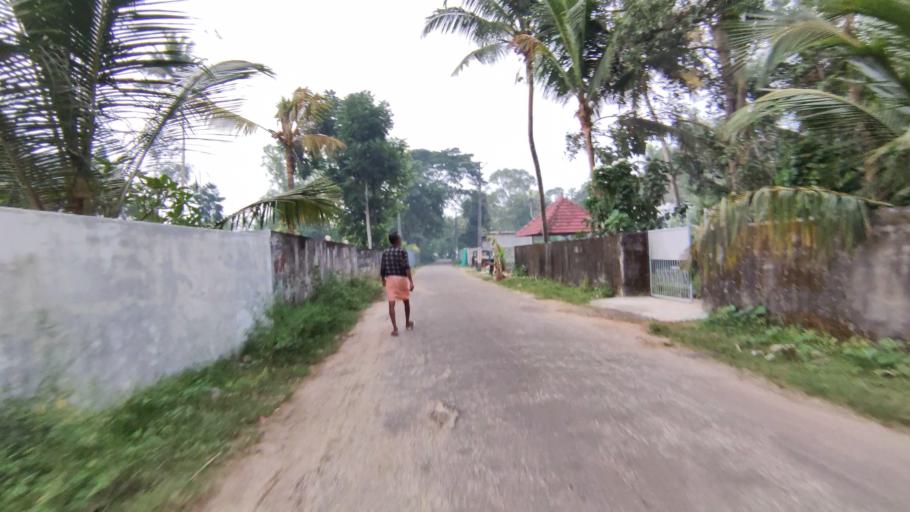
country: IN
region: Kerala
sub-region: Alappuzha
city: Shertallai
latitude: 9.6482
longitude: 76.3670
